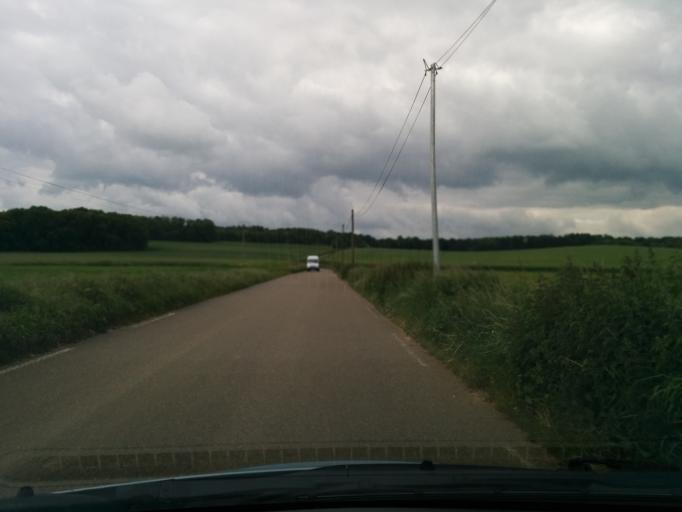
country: FR
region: Ile-de-France
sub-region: Departement des Yvelines
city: Gargenville
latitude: 49.0248
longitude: 1.8083
